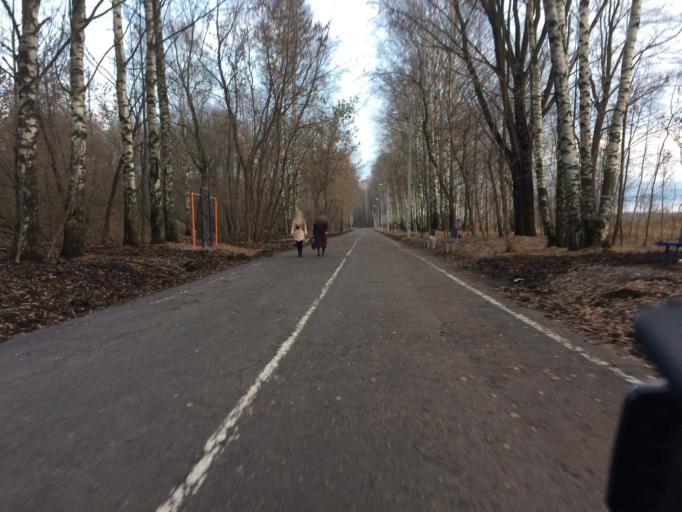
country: RU
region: Mariy-El
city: Yoshkar-Ola
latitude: 56.6239
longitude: 47.9127
